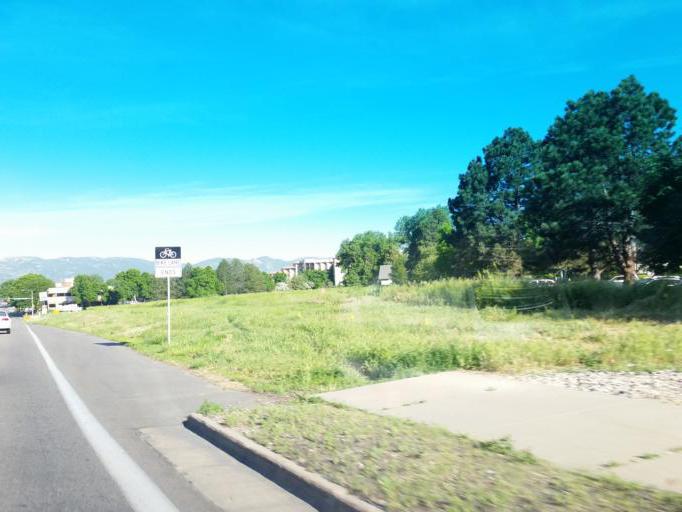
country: US
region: Colorado
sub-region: Larimer County
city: Fort Collins
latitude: 40.5381
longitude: -105.0673
